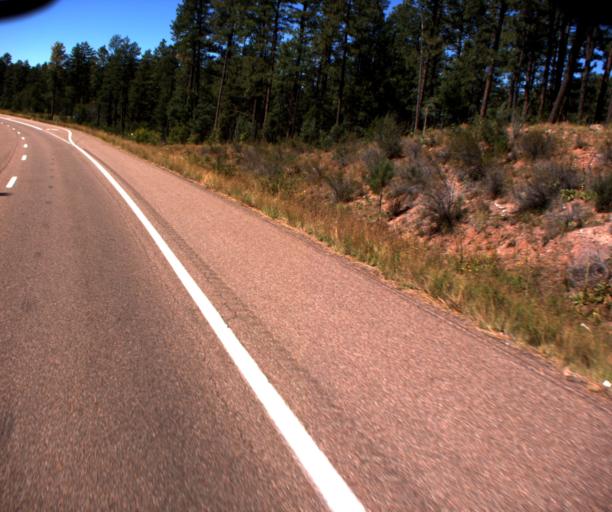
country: US
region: Arizona
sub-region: Gila County
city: Star Valley
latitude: 34.3136
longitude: -111.0033
